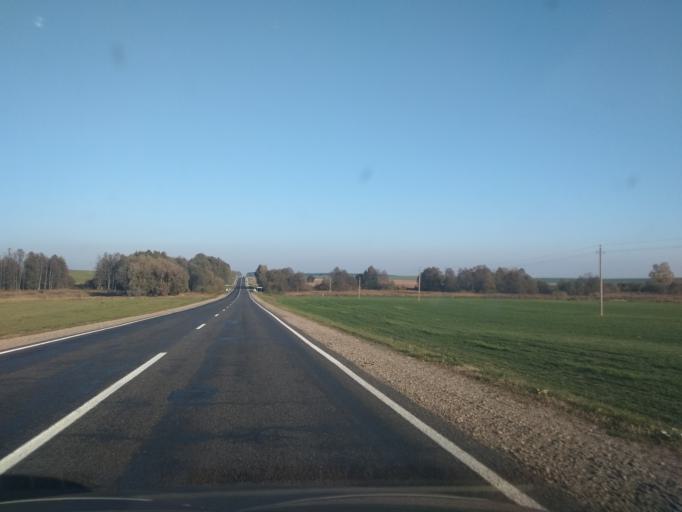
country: BY
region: Grodnenskaya
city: Svislach
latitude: 53.1335
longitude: 24.2215
